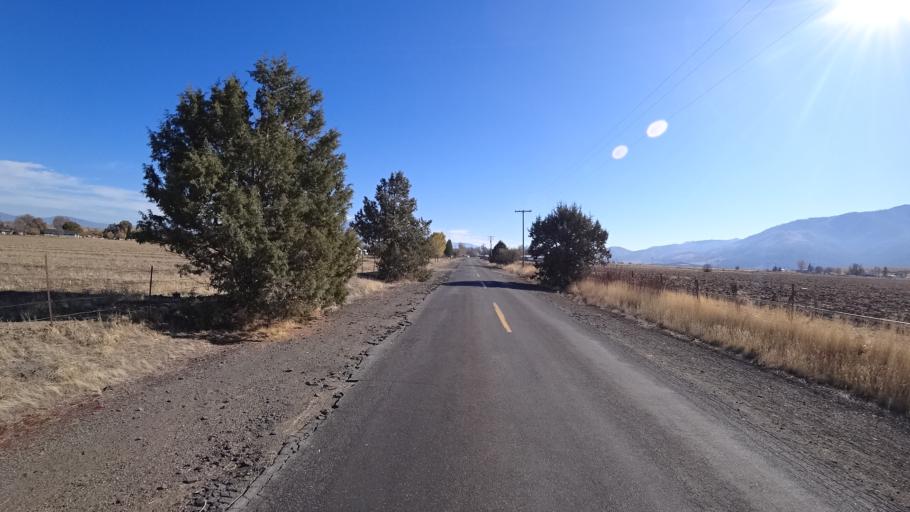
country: US
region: California
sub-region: Siskiyou County
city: Weed
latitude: 41.5224
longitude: -122.5259
